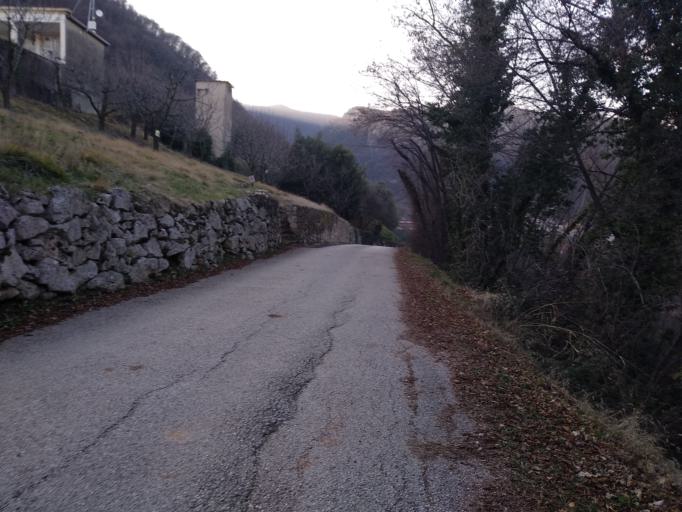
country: IT
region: Veneto
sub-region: Provincia di Vicenza
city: Lumignano
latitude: 45.4564
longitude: 11.5883
